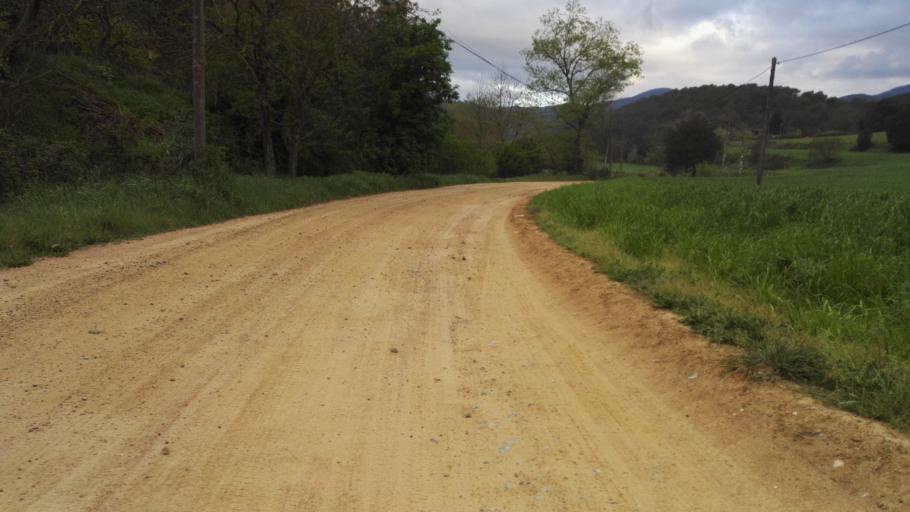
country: ES
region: Catalonia
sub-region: Provincia de Barcelona
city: Santa Maria de Palautordera
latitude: 41.6958
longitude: 2.4212
